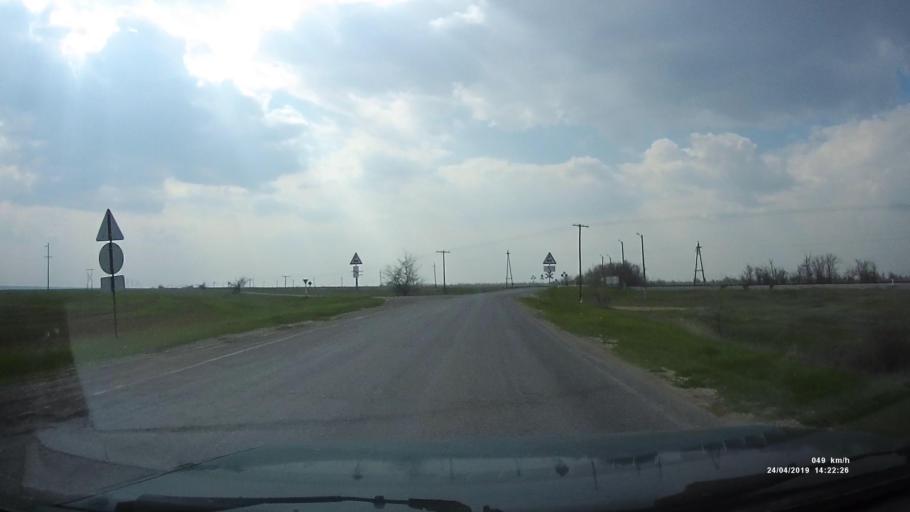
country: RU
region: Kalmykiya
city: Arshan'
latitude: 46.3172
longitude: 44.1236
